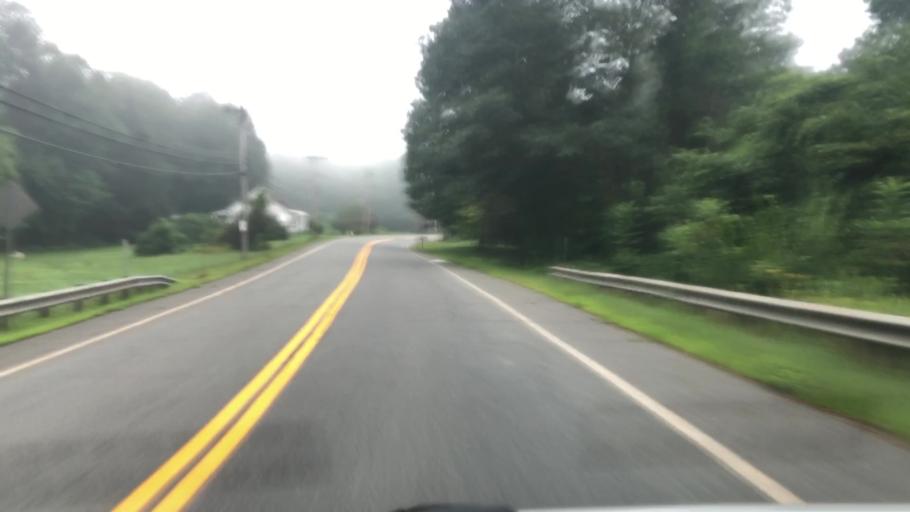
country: US
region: Massachusetts
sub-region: Franklin County
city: Buckland
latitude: 42.6130
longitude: -72.7693
